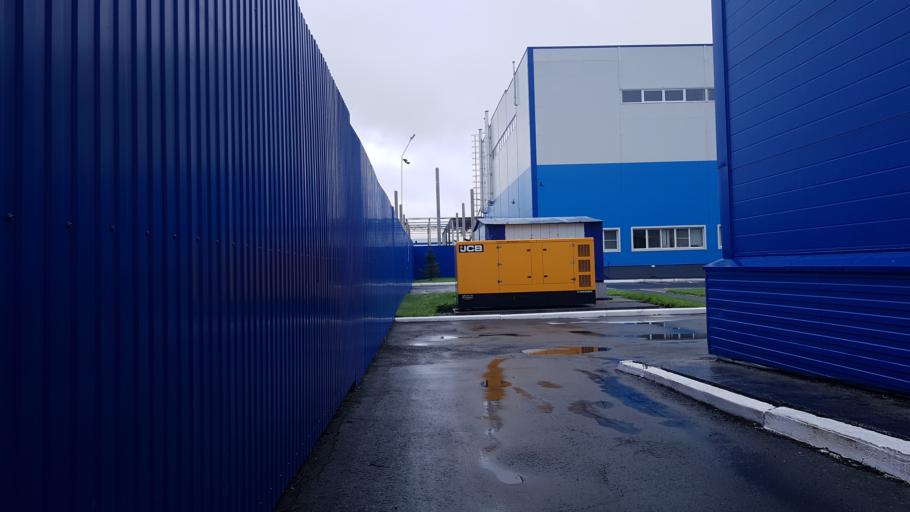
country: RU
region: Sverdlovsk
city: Sredneuralsk
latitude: 56.9960
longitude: 60.4757
